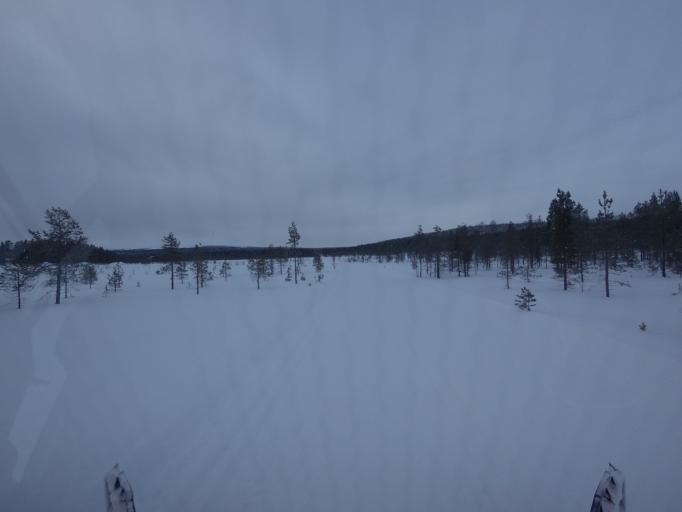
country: FI
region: Lapland
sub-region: Tunturi-Lappi
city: Kolari
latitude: 67.6181
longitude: 24.1314
